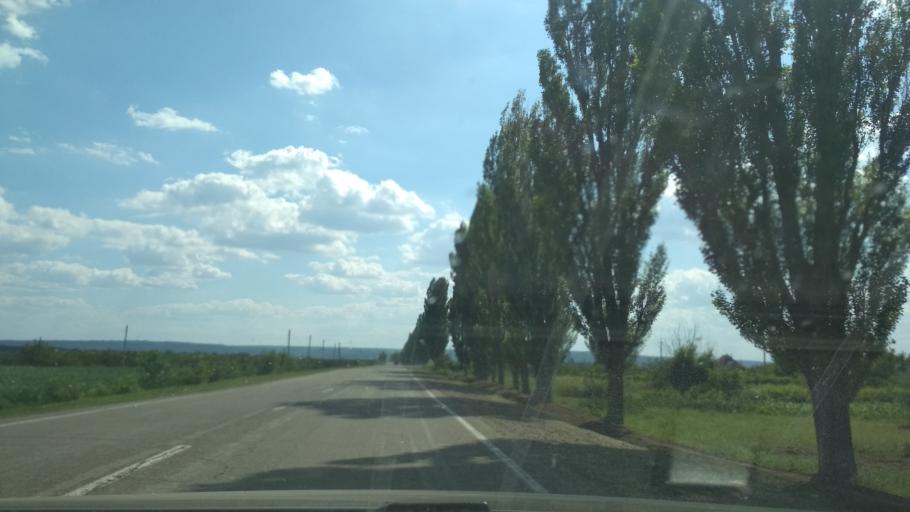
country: MD
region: Chisinau
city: Vadul lui Voda
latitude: 47.1343
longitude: 29.1301
